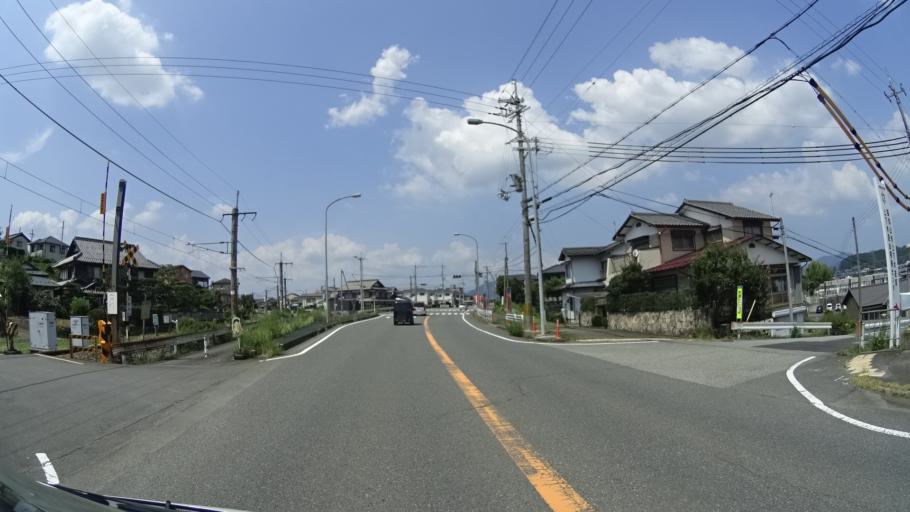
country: JP
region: Kyoto
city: Fukuchiyama
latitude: 35.2841
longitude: 135.1381
